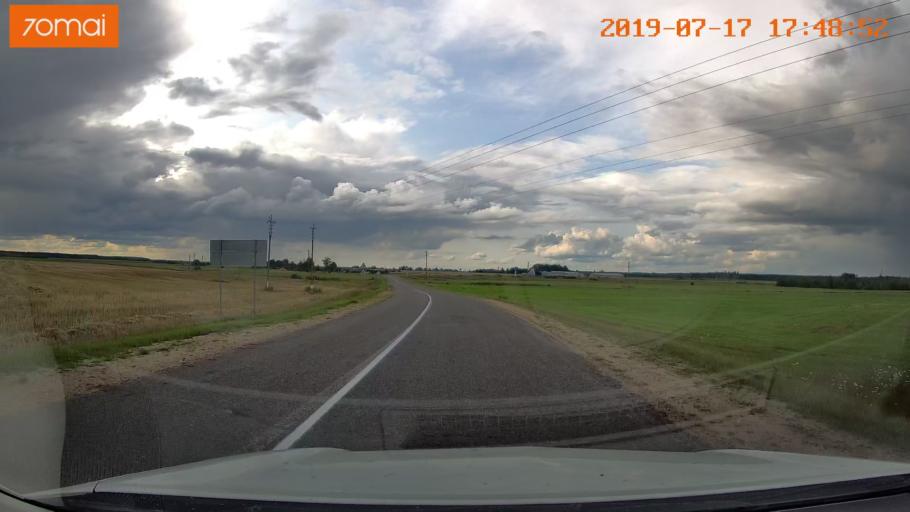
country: BY
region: Mogilev
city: Hlusha
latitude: 53.1278
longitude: 28.8189
